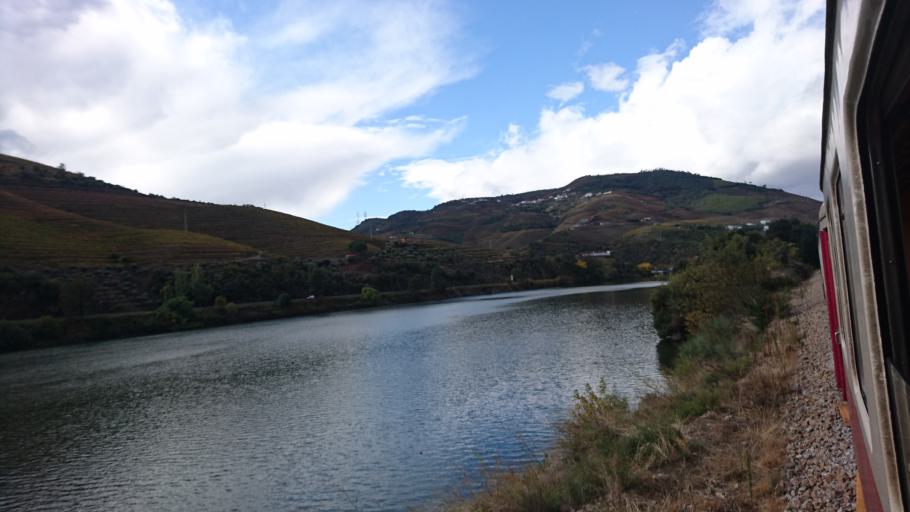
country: PT
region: Vila Real
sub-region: Sabrosa
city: Vilela
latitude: 41.1600
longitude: -7.6310
